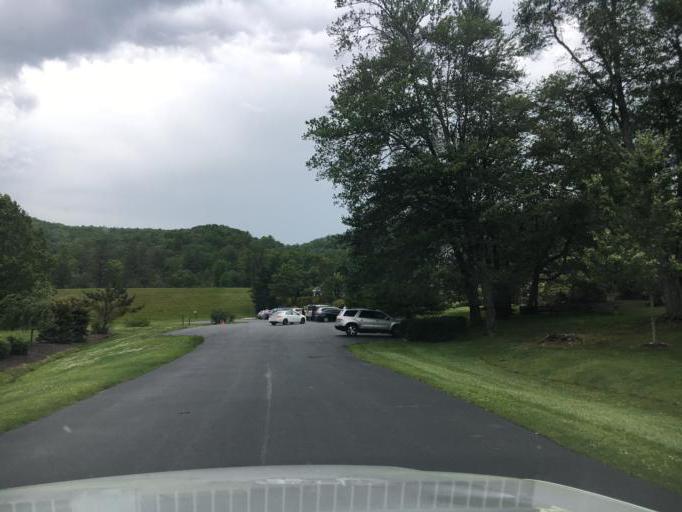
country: US
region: North Carolina
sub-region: Transylvania County
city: Brevard
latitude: 35.2498
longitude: -82.7282
